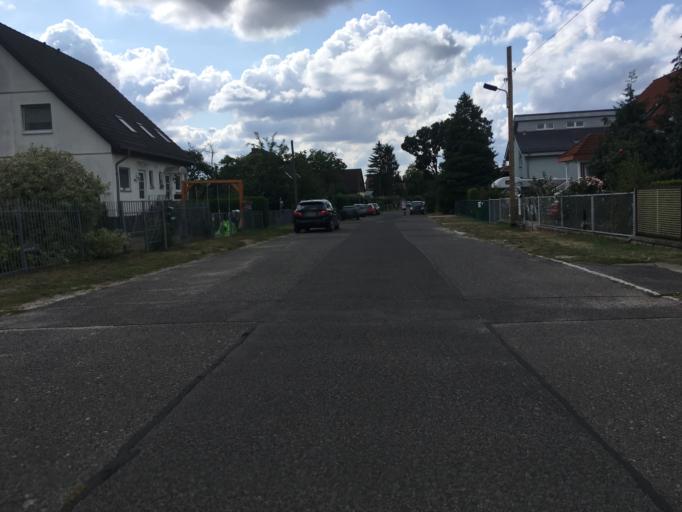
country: DE
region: Berlin
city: Karow
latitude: 52.6019
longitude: 13.4758
